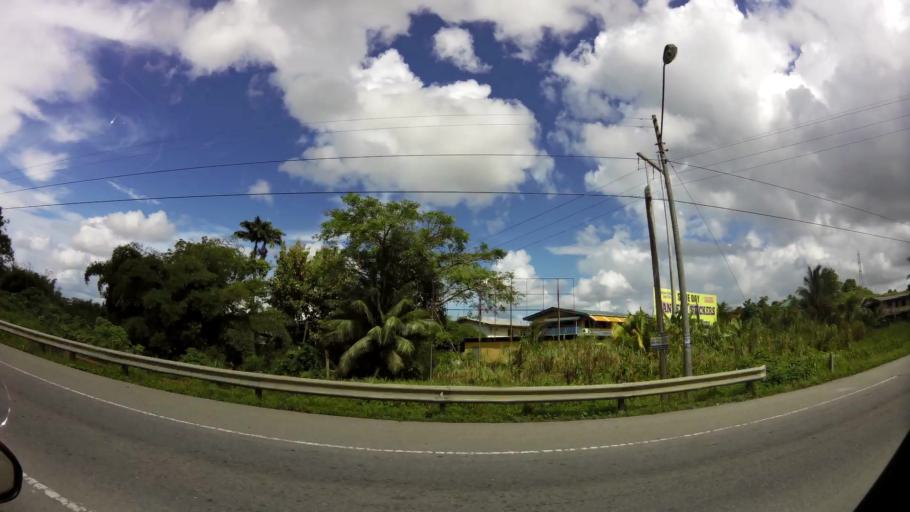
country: TT
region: City of San Fernando
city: Mon Repos
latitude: 10.2600
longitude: -61.4464
